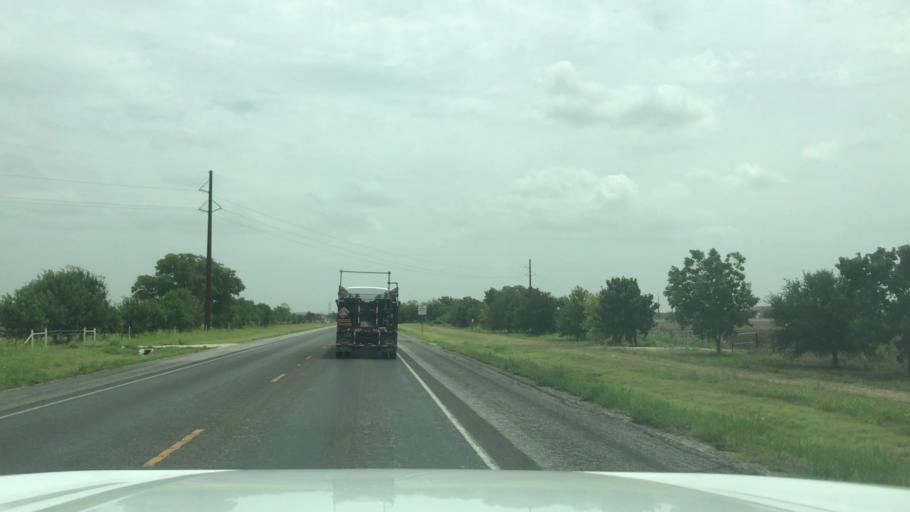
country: US
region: Texas
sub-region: Bosque County
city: Clifton
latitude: 31.7991
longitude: -97.5957
